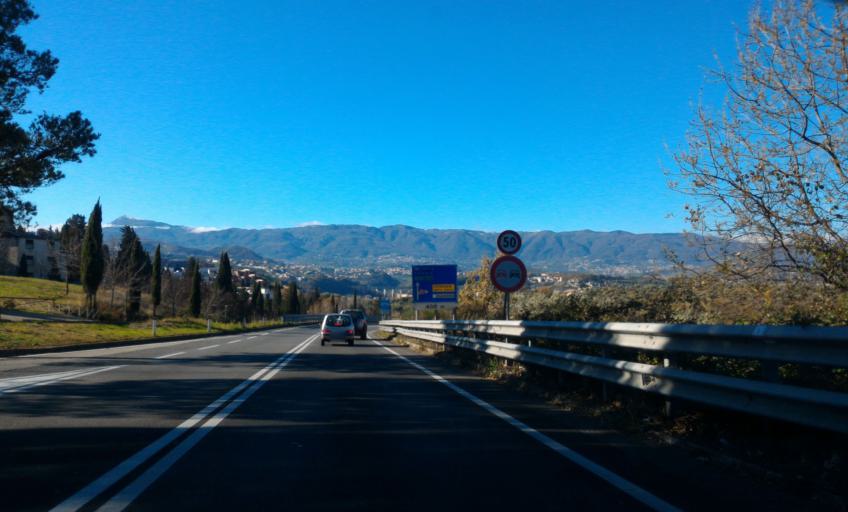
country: IT
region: Calabria
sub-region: Provincia di Cosenza
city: Cosenza
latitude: 39.2950
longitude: 16.2741
